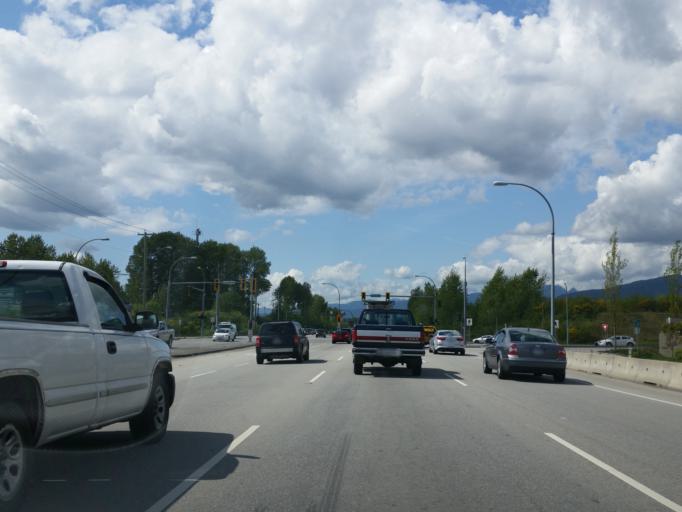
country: CA
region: British Columbia
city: Coquitlam
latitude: 49.2527
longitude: -122.7409
